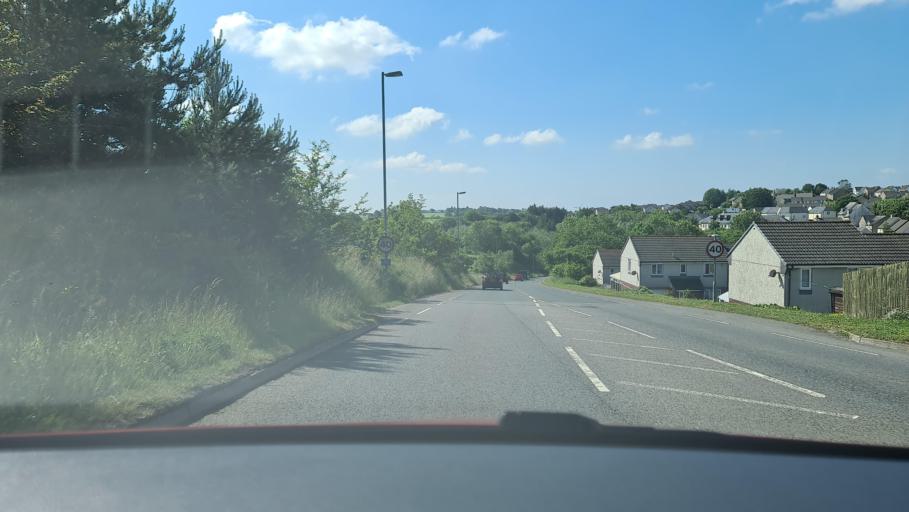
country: GB
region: England
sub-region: Cornwall
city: Liskeard
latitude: 50.4577
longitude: -4.4500
